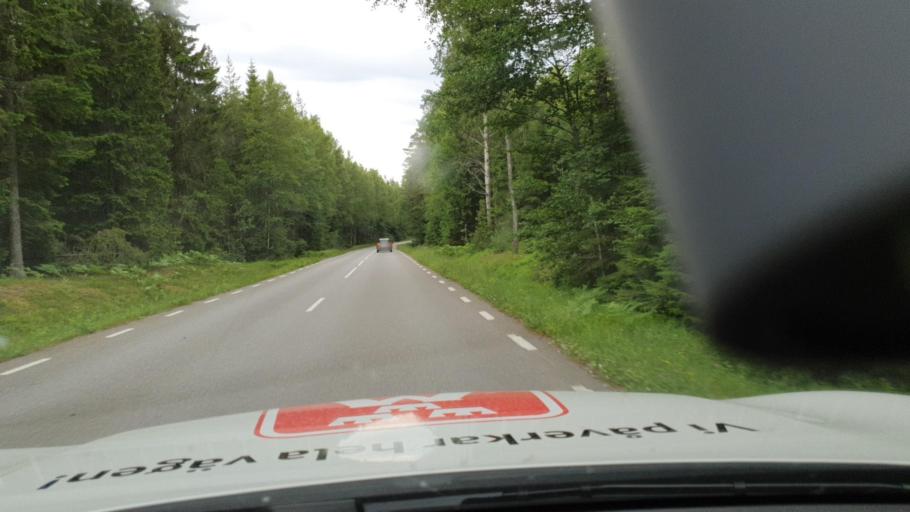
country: SE
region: Vaestra Goetaland
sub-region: Karlsborgs Kommun
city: Karlsborg
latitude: 58.7425
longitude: 14.5056
